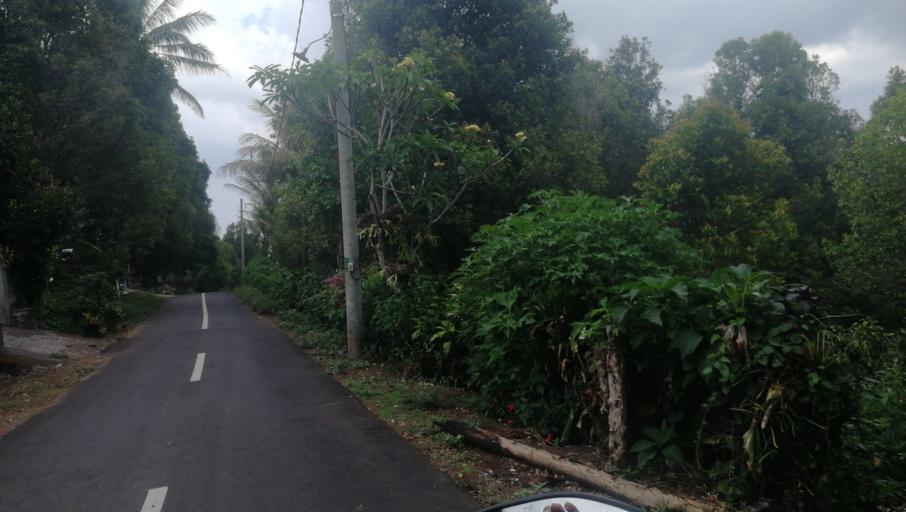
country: ID
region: Bali
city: Munduk
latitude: -8.2991
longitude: 115.0539
